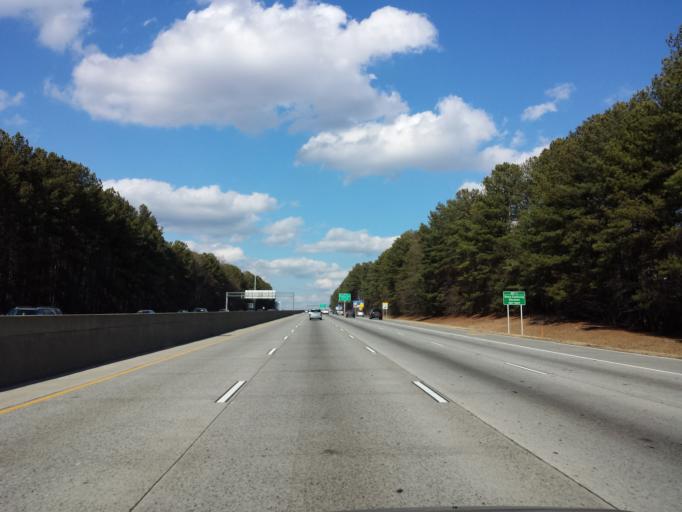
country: US
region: Georgia
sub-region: Fulton County
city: Alpharetta
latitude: 34.0774
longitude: -84.2673
